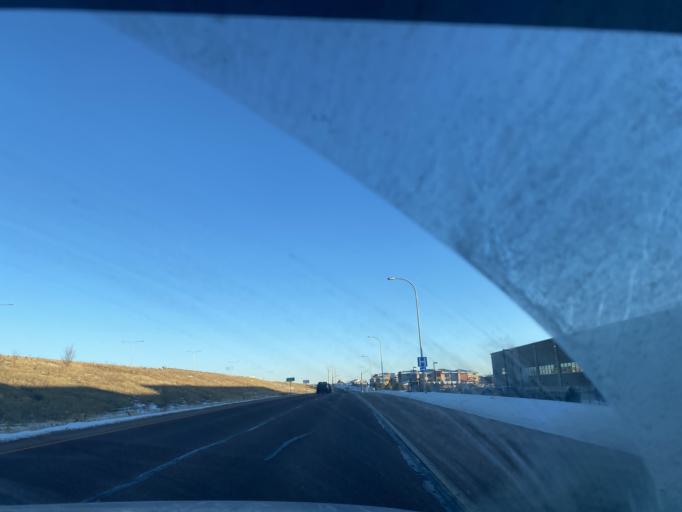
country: US
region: Colorado
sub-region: El Paso County
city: Black Forest
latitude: 38.9699
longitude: -104.7463
